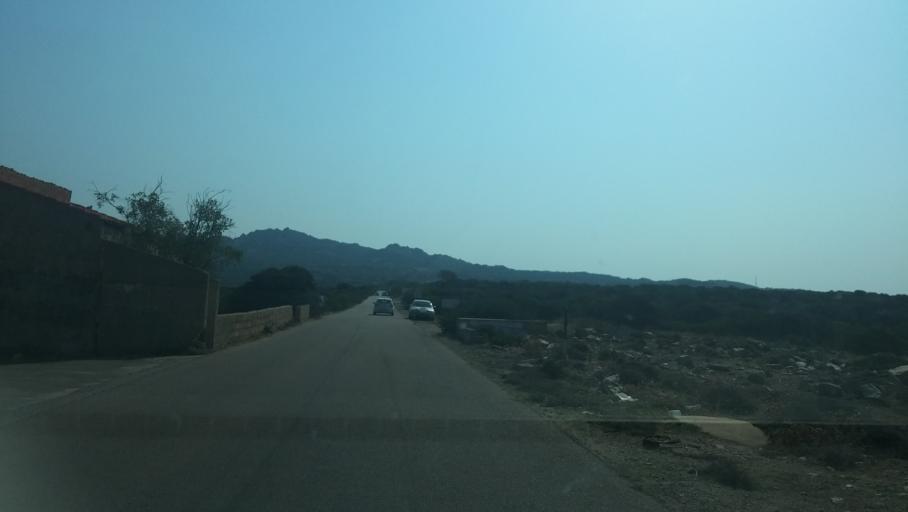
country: IT
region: Sardinia
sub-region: Provincia di Olbia-Tempio
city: La Maddalena
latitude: 41.2155
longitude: 9.4460
